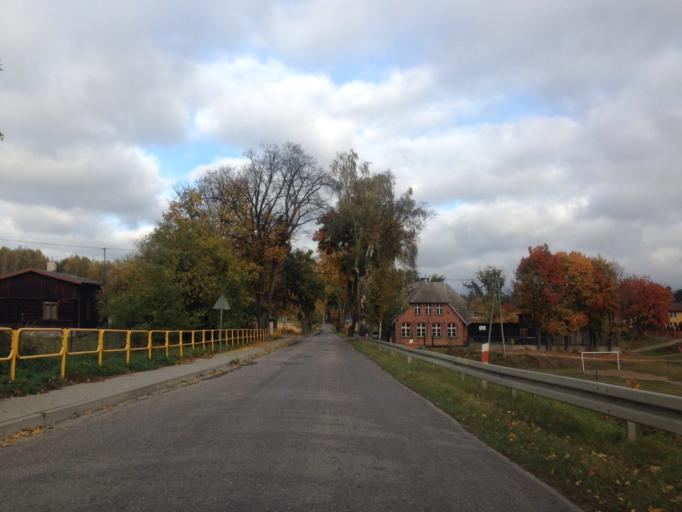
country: PL
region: Kujawsko-Pomorskie
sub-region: Powiat brodnicki
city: Bartniczka
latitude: 53.2303
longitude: 19.6313
